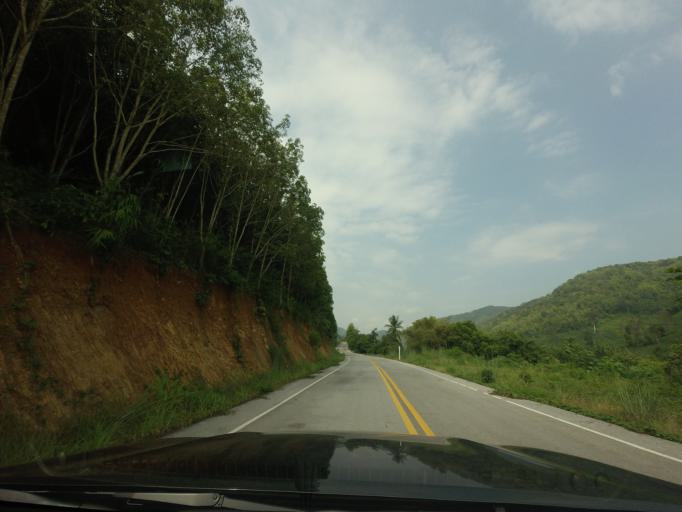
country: LA
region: Xiagnabouli
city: Muang Kenthao
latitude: 17.7741
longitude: 101.5364
